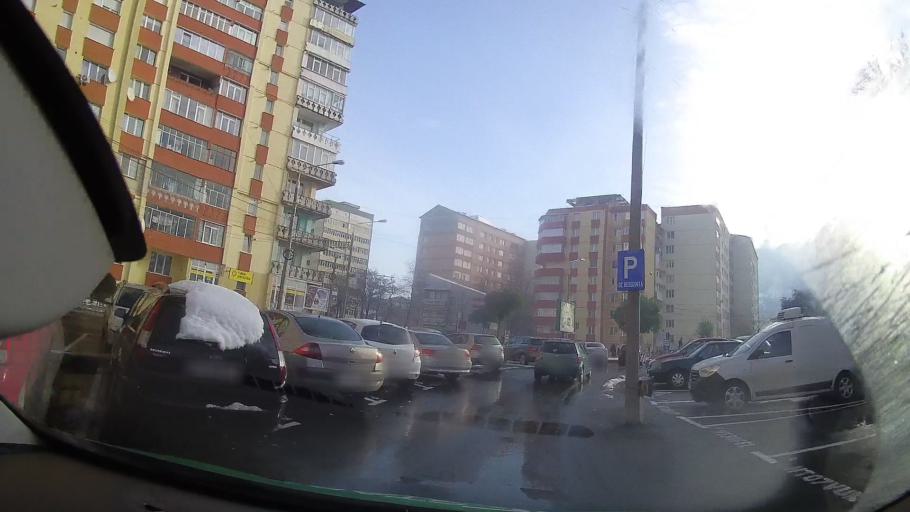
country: RO
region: Neamt
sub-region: Municipiul Piatra-Neamt
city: Valeni
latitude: 46.9369
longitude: 26.3809
